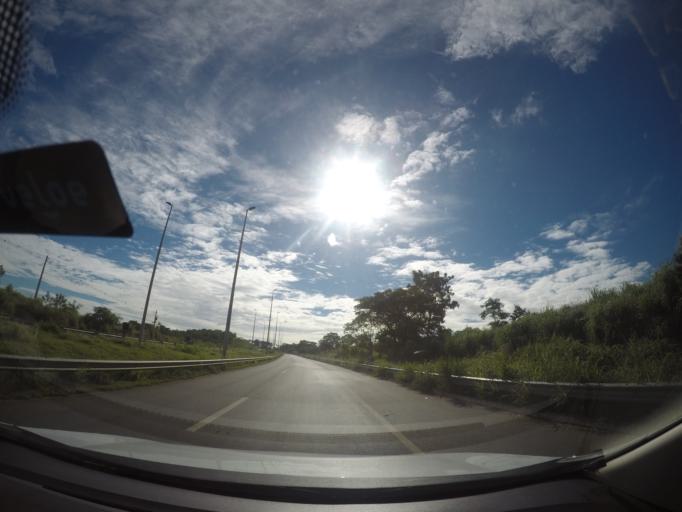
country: BR
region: Goias
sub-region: Senador Canedo
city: Senador Canedo
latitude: -16.6903
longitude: -49.1708
